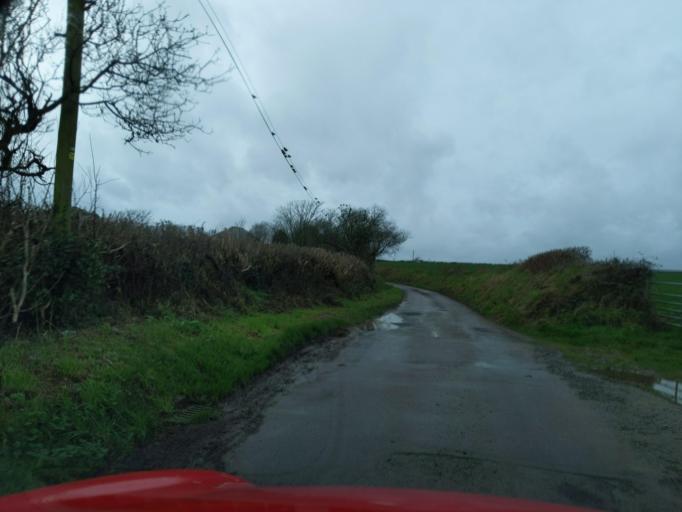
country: GB
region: England
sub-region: Cornwall
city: Duloe
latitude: 50.3497
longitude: -4.5491
